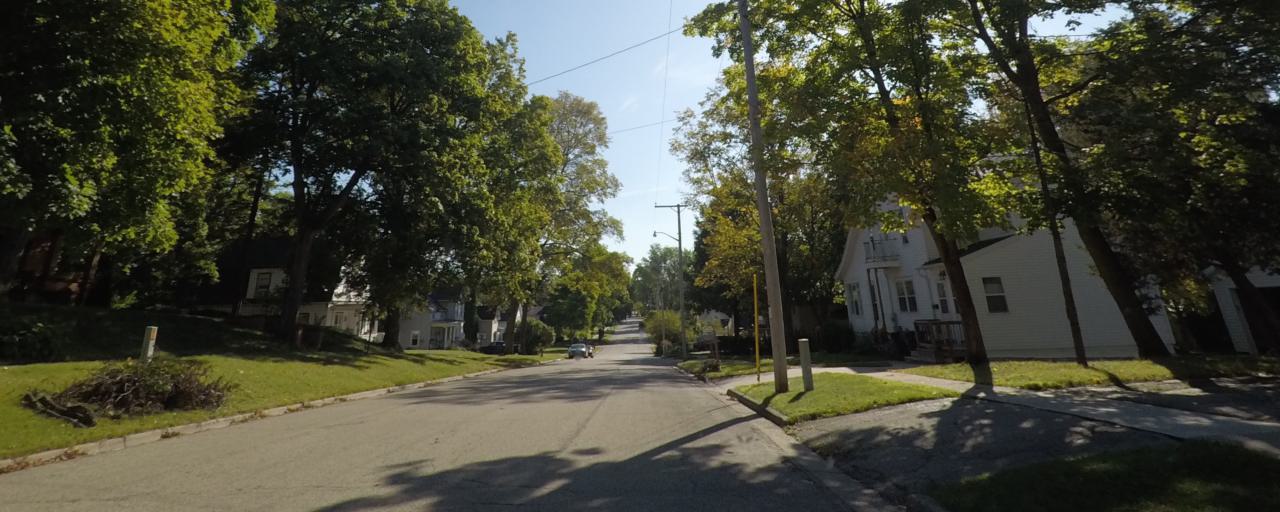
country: US
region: Wisconsin
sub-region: Jefferson County
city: Jefferson
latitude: 43.0079
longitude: -88.8020
